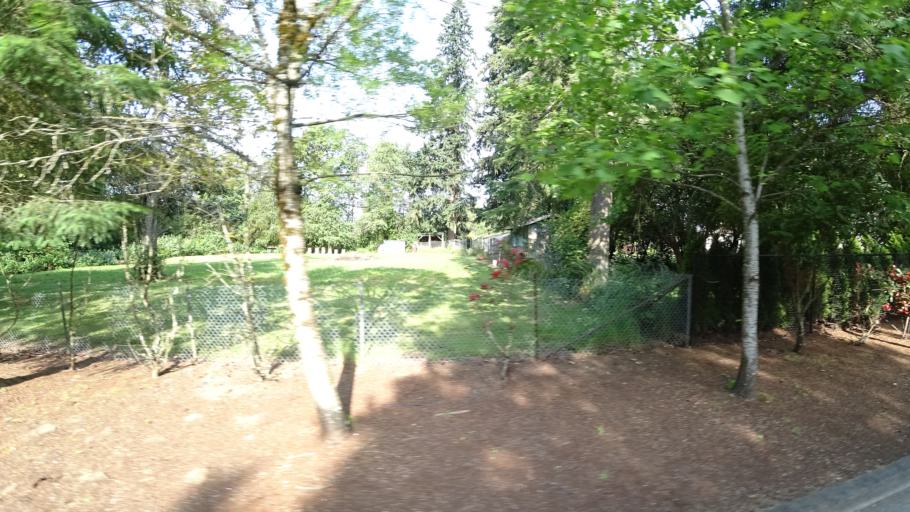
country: US
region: Oregon
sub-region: Clackamas County
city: Happy Valley
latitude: 45.4444
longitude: -122.5276
